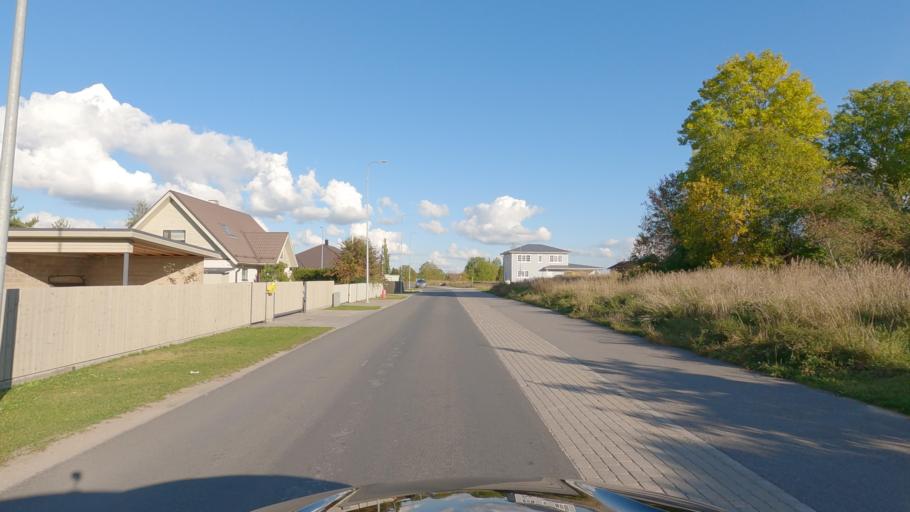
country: EE
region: Harju
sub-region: Saue vald
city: Laagri
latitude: 59.3482
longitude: 24.6328
